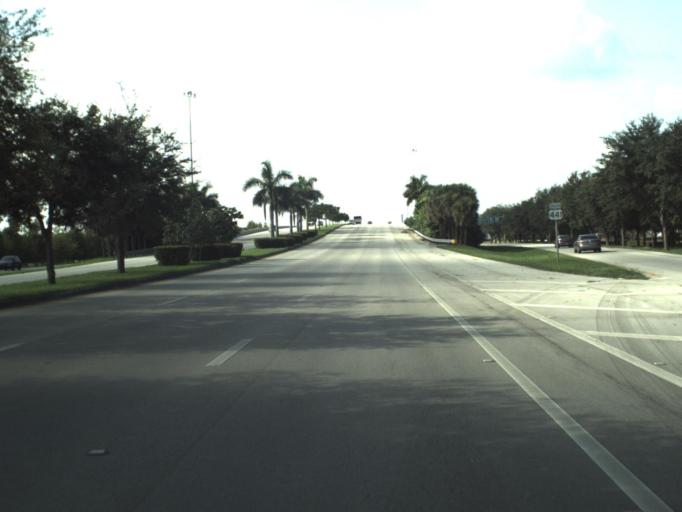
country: US
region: Florida
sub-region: Broward County
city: Margate
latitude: 26.2777
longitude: -80.2020
